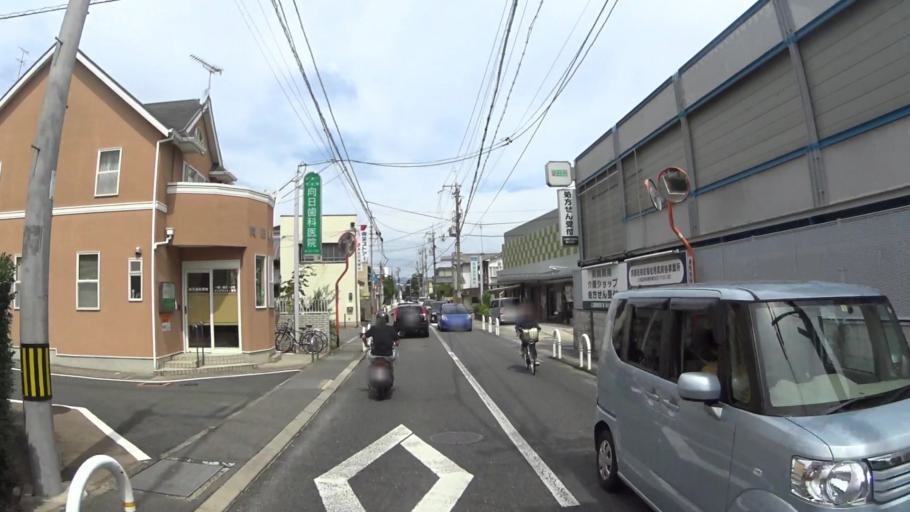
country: JP
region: Kyoto
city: Muko
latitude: 34.9501
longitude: 135.6989
